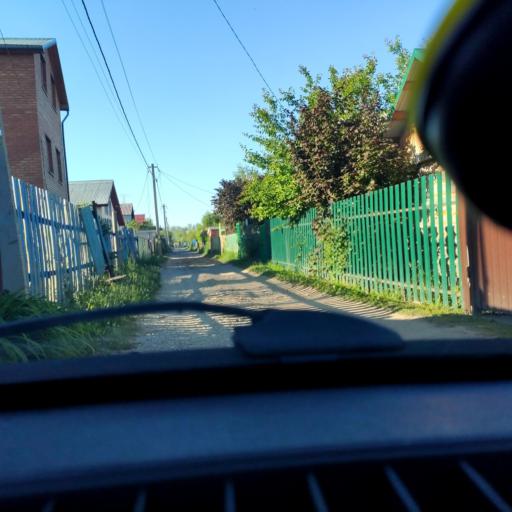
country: RU
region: Samara
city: Tol'yatti
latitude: 53.5937
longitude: 49.3145
